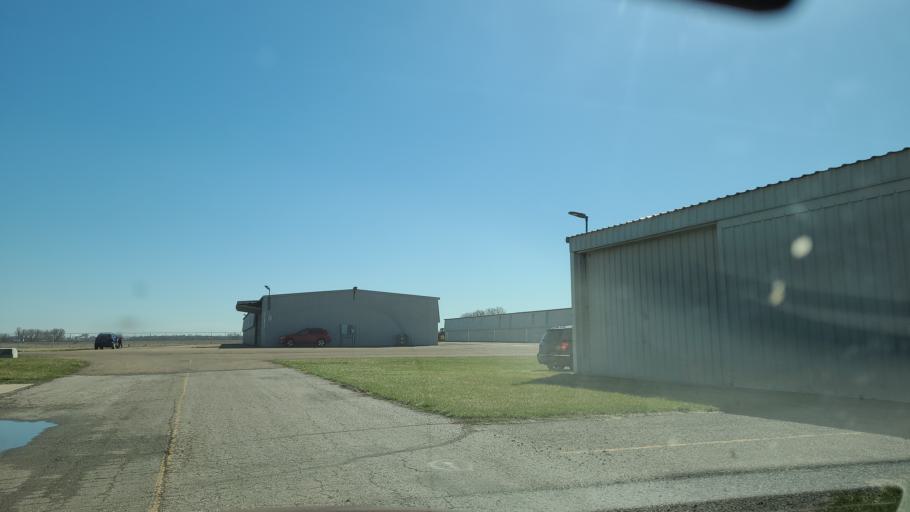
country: US
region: Kansas
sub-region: Douglas County
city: Lawrence
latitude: 39.0047
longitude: -95.2179
